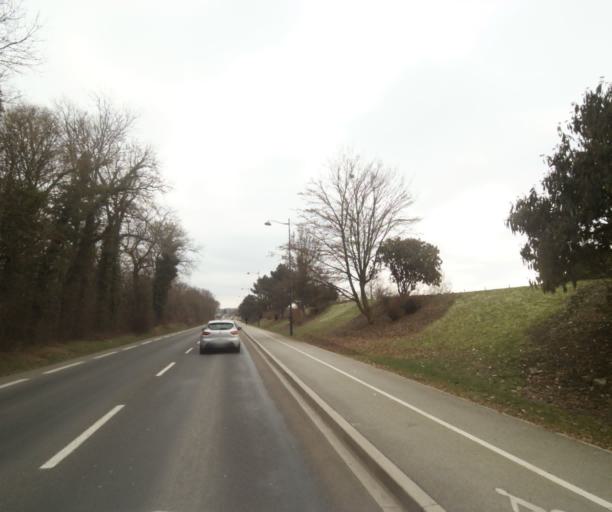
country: FR
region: Champagne-Ardenne
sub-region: Departement de la Haute-Marne
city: Bettancourt-la-Ferree
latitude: 48.6261
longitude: 4.9769
